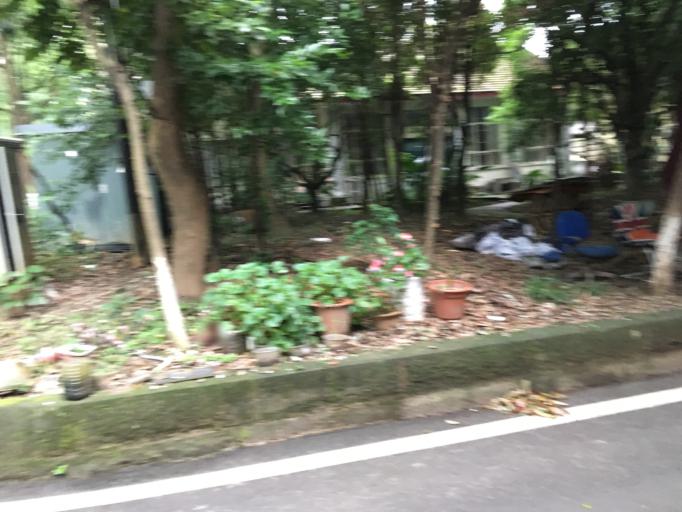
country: CN
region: Chongqing Shi
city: Beiwenquan
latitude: 29.8227
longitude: 106.4200
